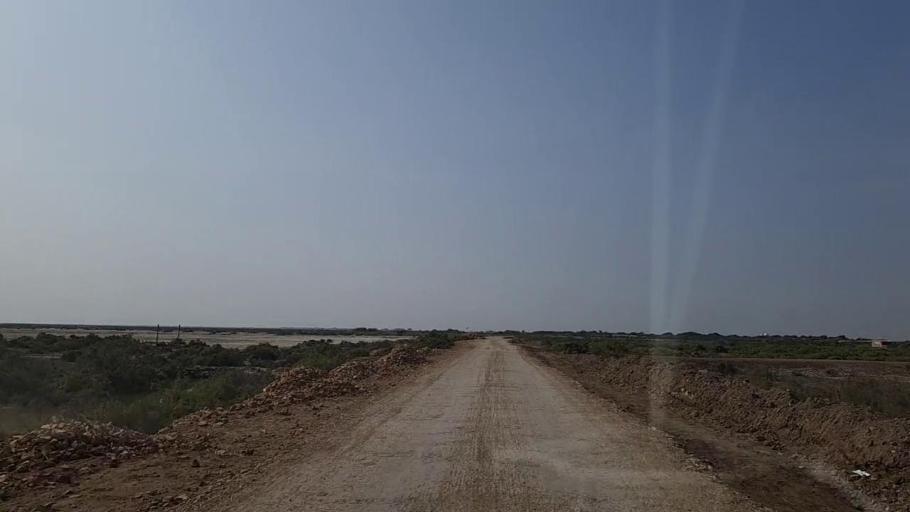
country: PK
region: Sindh
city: Chuhar Jamali
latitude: 24.1995
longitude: 67.8275
